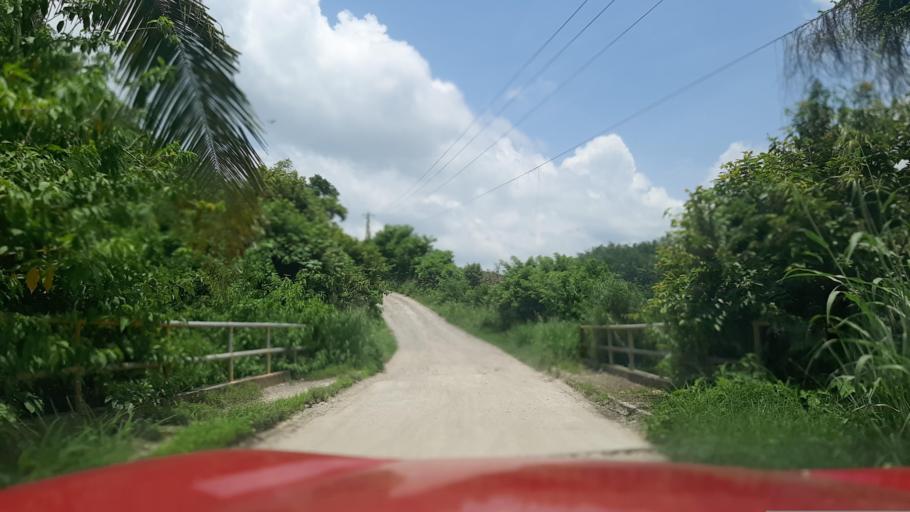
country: MX
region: Veracruz
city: Papantla de Olarte
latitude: 20.4385
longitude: -97.2782
